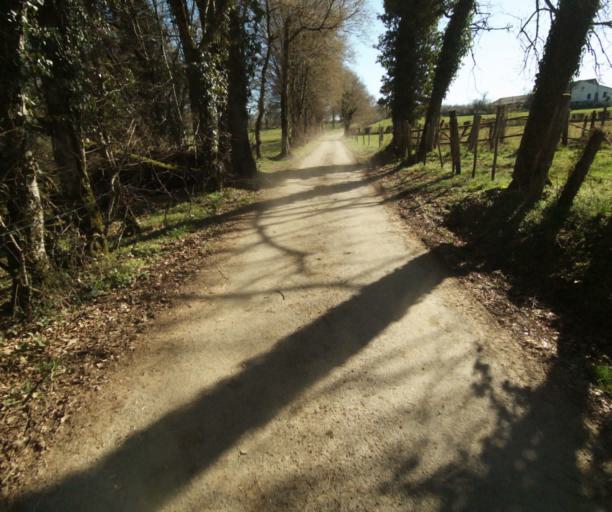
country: FR
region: Limousin
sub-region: Departement de la Correze
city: Chamboulive
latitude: 45.4331
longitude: 1.6510
